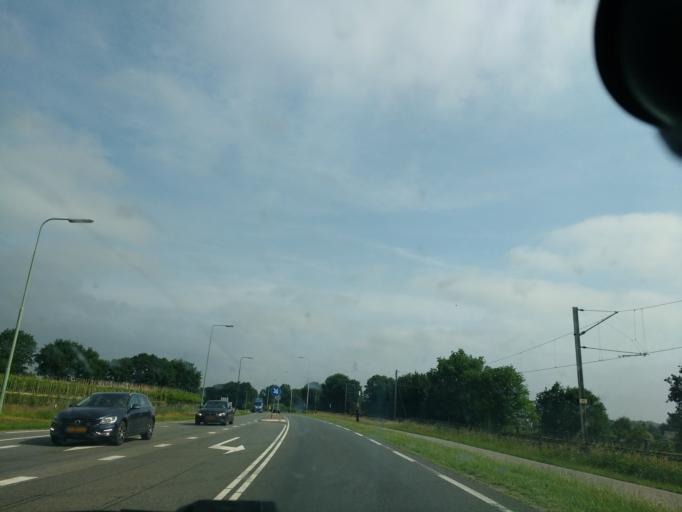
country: NL
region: Utrecht
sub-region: Gemeente Rhenen
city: Rhenen
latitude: 51.9668
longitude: 5.5800
